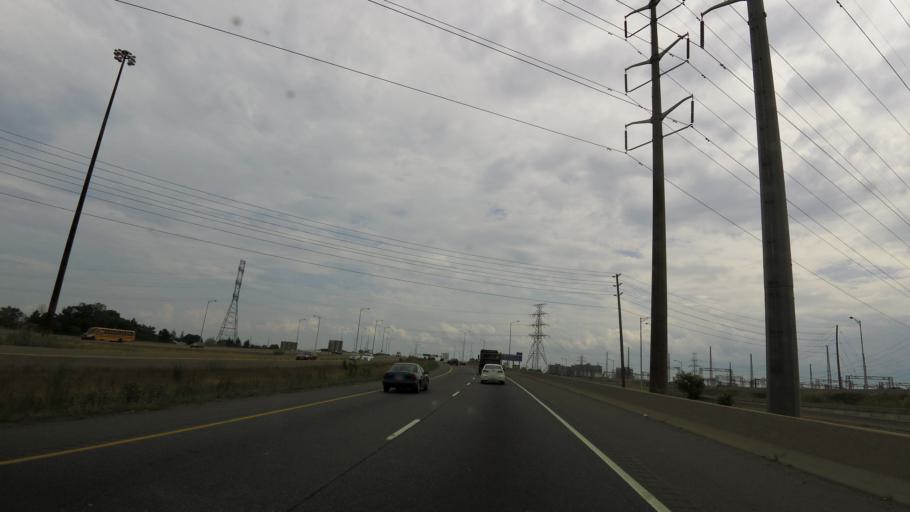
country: CA
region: Ontario
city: Burlington
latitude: 43.3341
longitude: -79.8293
